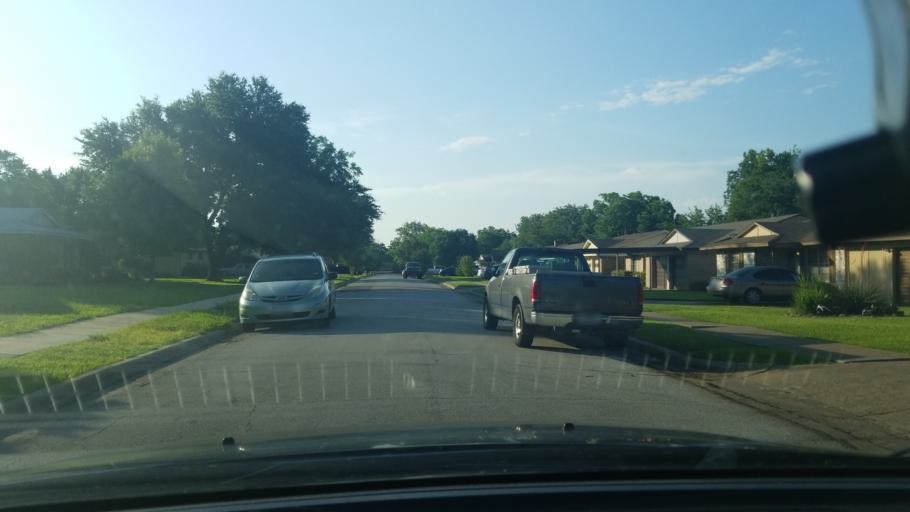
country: US
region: Texas
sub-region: Dallas County
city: Mesquite
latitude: 32.8038
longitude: -96.6429
